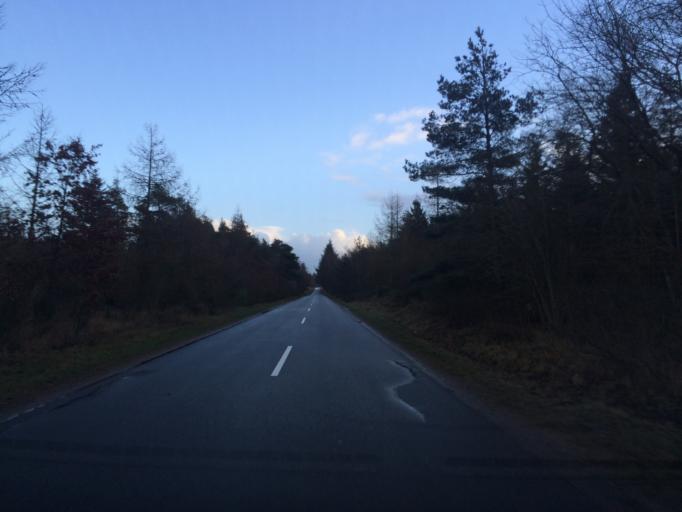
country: DK
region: Central Jutland
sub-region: Holstebro Kommune
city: Ulfborg
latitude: 56.2500
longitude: 8.3711
